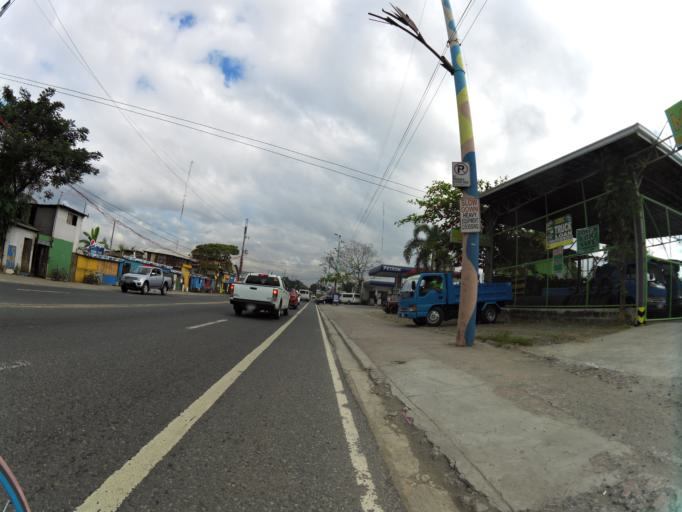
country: PH
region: Metro Manila
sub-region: Marikina
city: Calumpang
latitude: 14.6393
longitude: 121.1029
